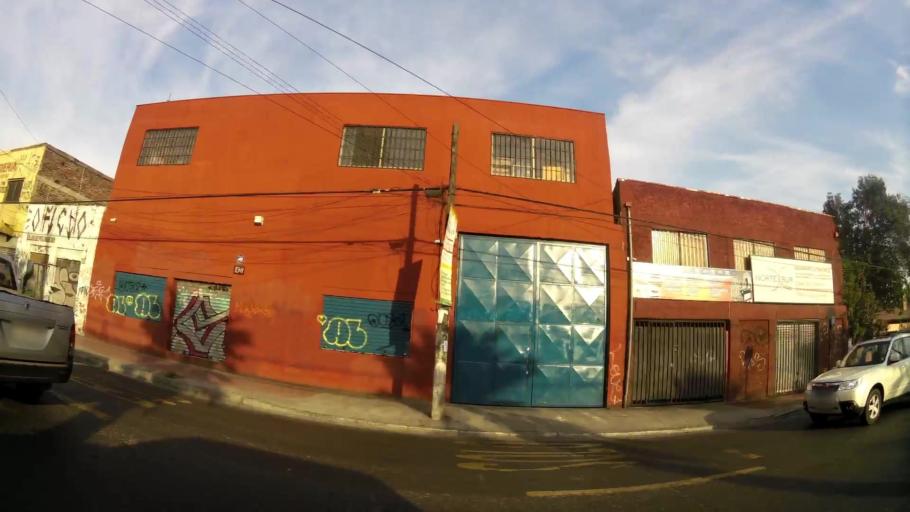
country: CL
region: Santiago Metropolitan
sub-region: Provincia de Santiago
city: La Pintana
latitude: -33.5311
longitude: -70.6628
